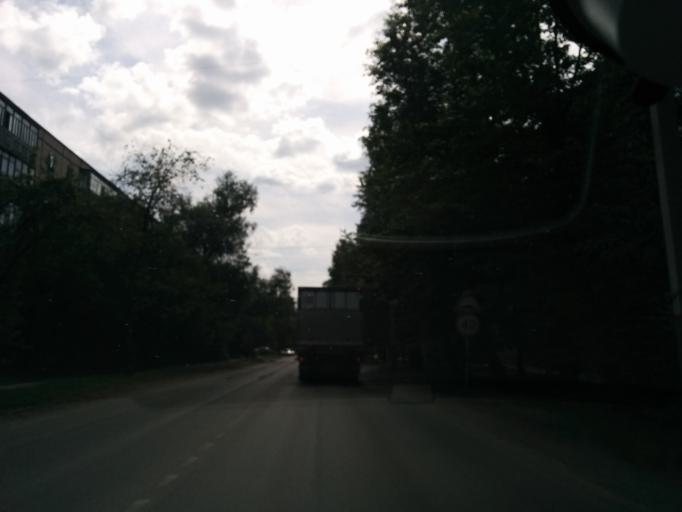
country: RU
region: Perm
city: Overyata
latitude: 58.0186
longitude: 55.9770
